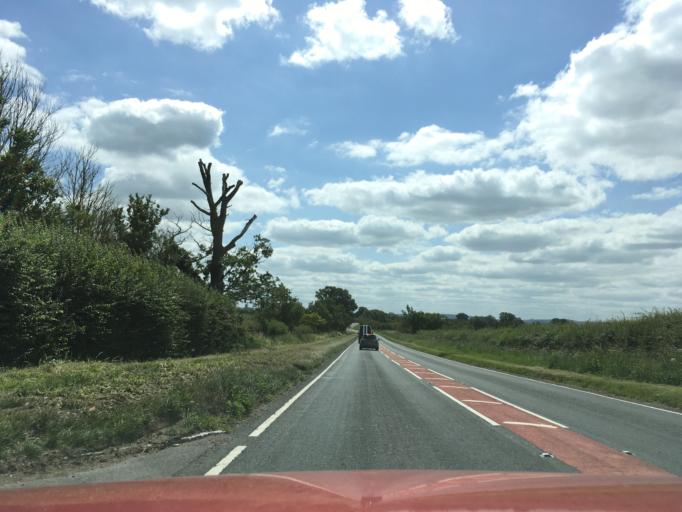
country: GB
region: England
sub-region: Buckinghamshire
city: Aylesbury
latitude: 51.8474
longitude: -0.8245
